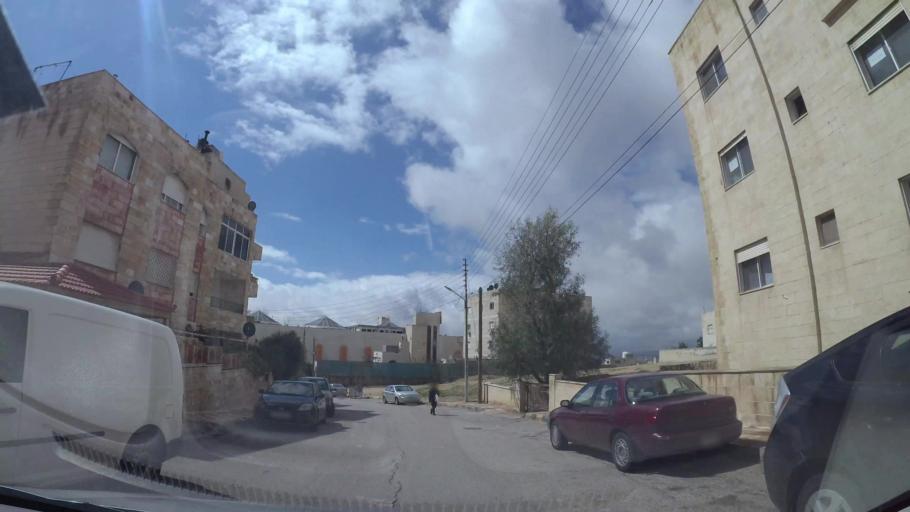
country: JO
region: Amman
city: Al Jubayhah
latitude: 32.0587
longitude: 35.8726
